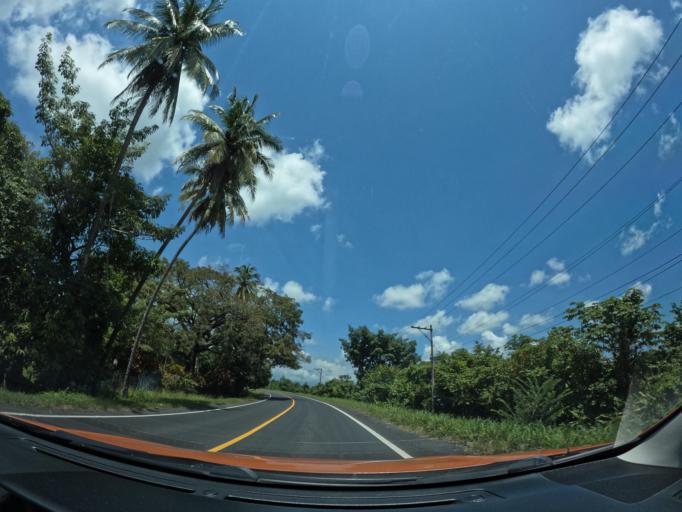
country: GT
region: Escuintla
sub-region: Municipio de Masagua
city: Masagua
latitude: 14.1562
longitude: -90.8804
